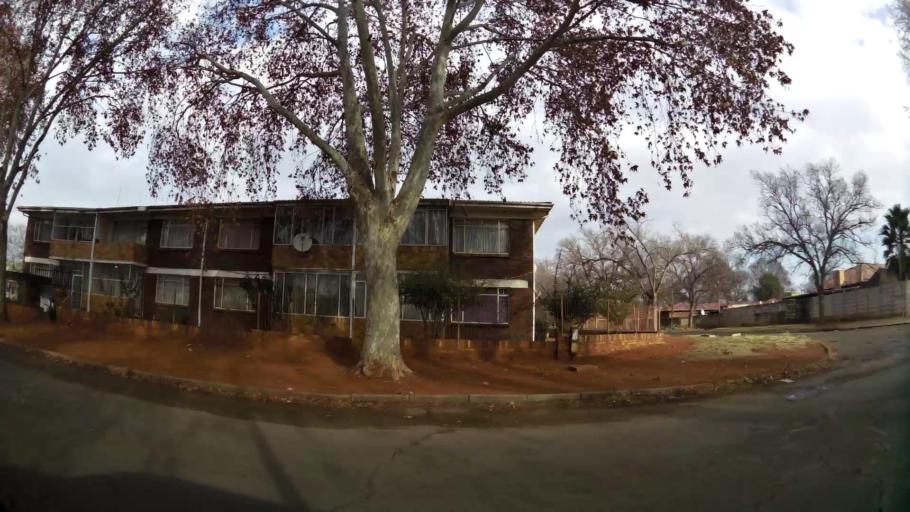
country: ZA
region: Gauteng
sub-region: Sedibeng District Municipality
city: Vanderbijlpark
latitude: -26.7013
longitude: 27.8159
